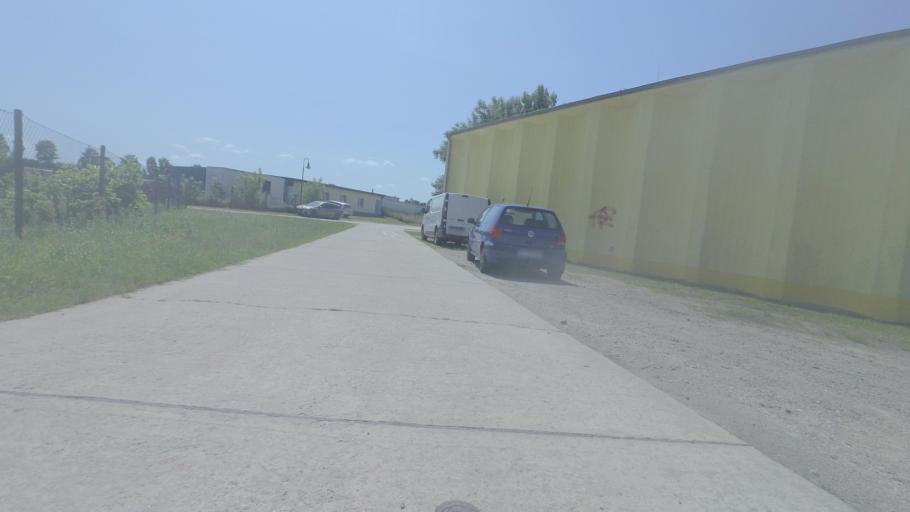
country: DE
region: Brandenburg
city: Rangsdorf
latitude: 52.2572
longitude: 13.3815
